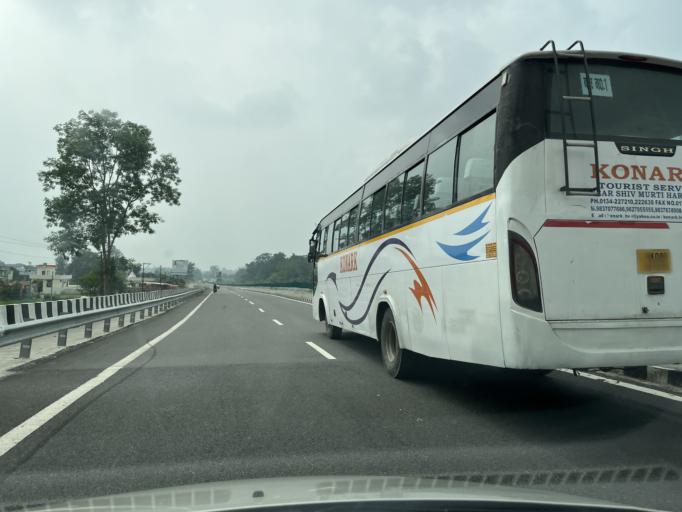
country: IN
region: Uttarakhand
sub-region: Dehradun
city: Raiwala
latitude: 30.0657
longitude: 78.2092
